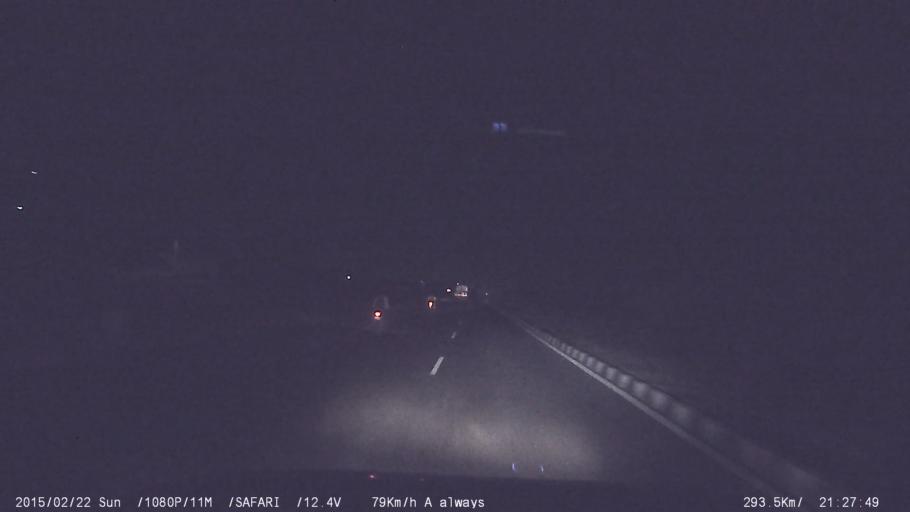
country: IN
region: Tamil Nadu
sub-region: Karur
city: Karur
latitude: 10.9191
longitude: 78.0439
